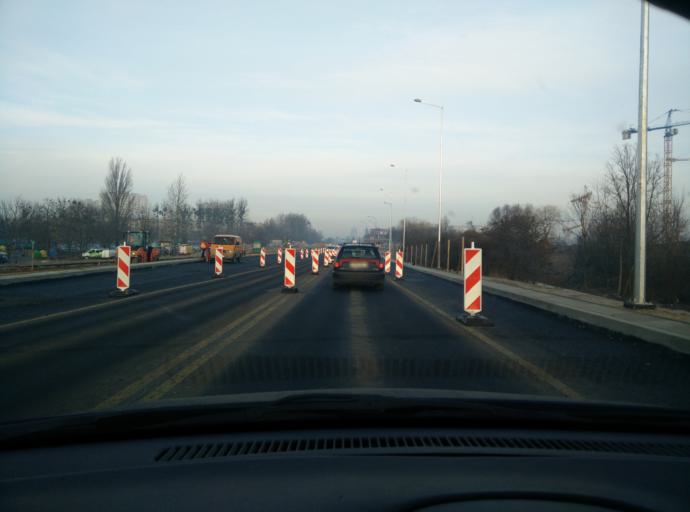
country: PL
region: Greater Poland Voivodeship
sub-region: Poznan
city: Poznan
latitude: 52.3929
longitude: 16.9594
